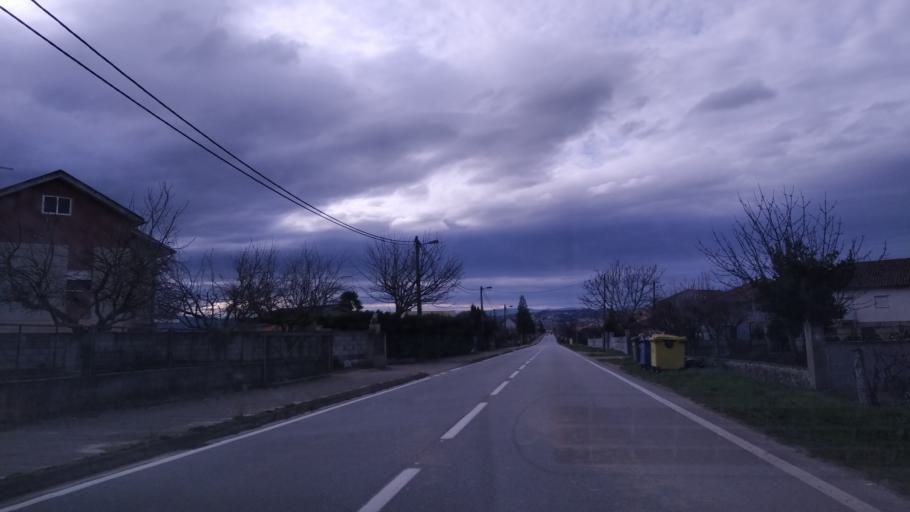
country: PT
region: Vila Real
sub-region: Chaves
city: Chaves
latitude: 41.7460
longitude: -7.4364
